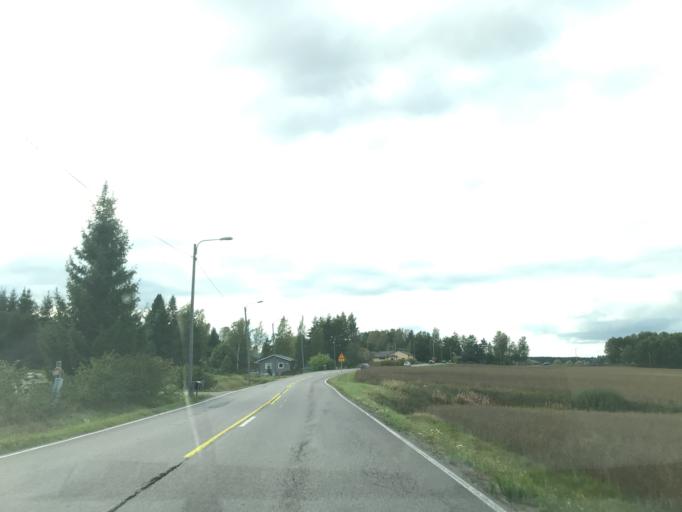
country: FI
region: Uusimaa
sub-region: Helsinki
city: Kirkkonummi
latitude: 60.2443
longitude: 24.4491
